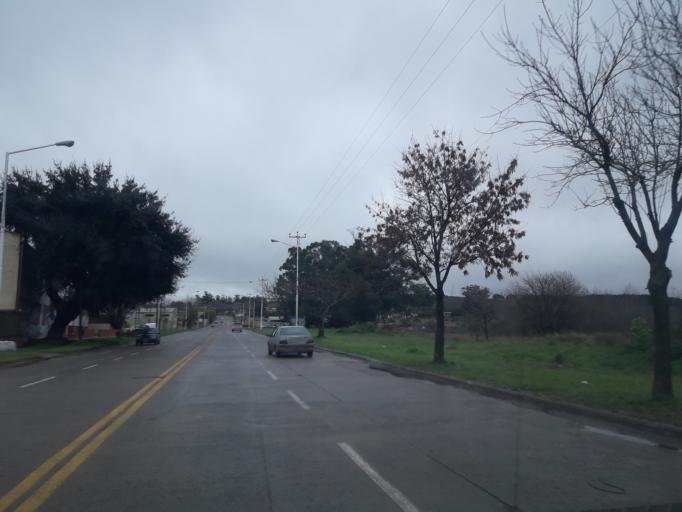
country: AR
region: Buenos Aires
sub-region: Partido de Tandil
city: Tandil
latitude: -37.3214
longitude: -59.1653
